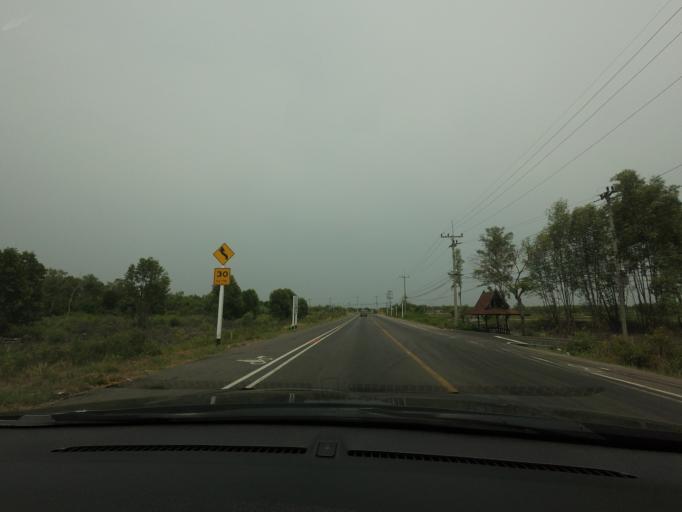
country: TH
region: Phetchaburi
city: Ban Laem
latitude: 13.2887
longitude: 99.9211
